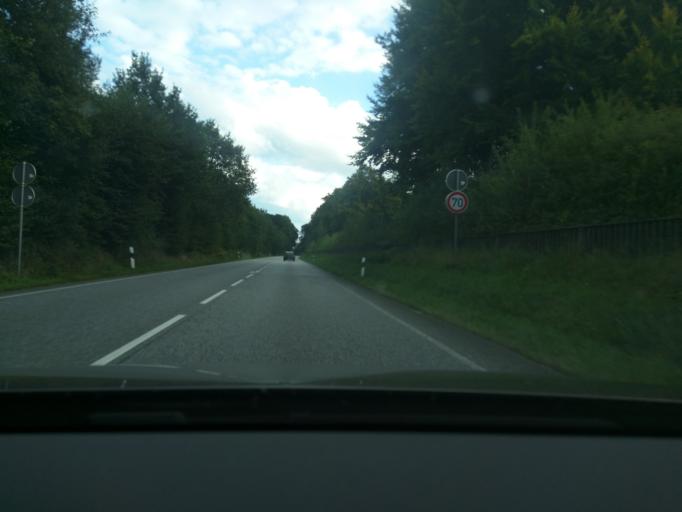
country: DE
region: Schleswig-Holstein
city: Kasseburg
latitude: 53.5524
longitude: 10.4150
